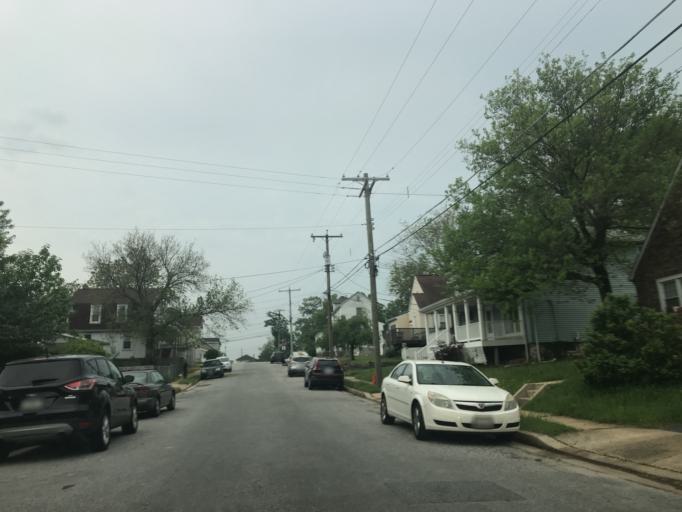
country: US
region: Maryland
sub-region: Baltimore County
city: Parkville
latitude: 39.3753
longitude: -76.5433
